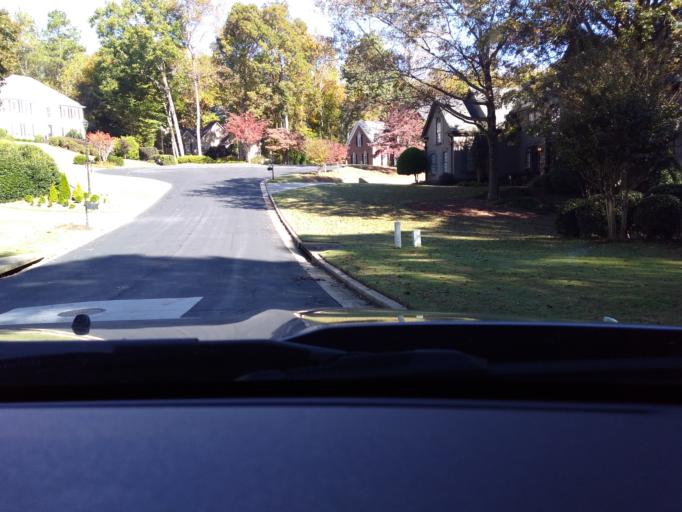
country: US
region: Georgia
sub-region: Fulton County
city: Johns Creek
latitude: 34.0215
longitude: -84.1878
